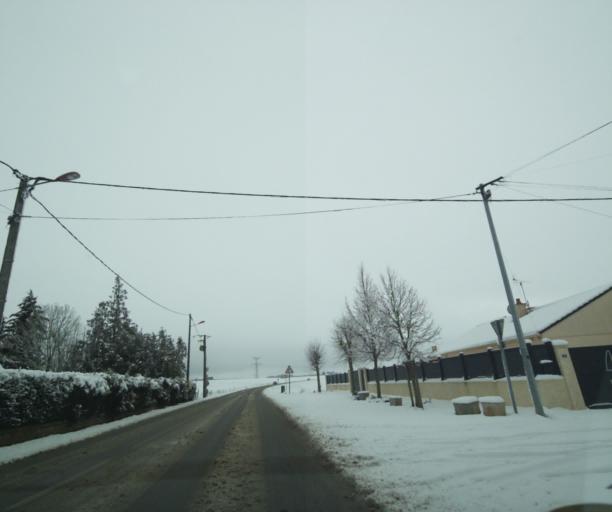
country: FR
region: Champagne-Ardenne
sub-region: Departement de la Haute-Marne
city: Wassy
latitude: 48.5236
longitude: 4.9309
